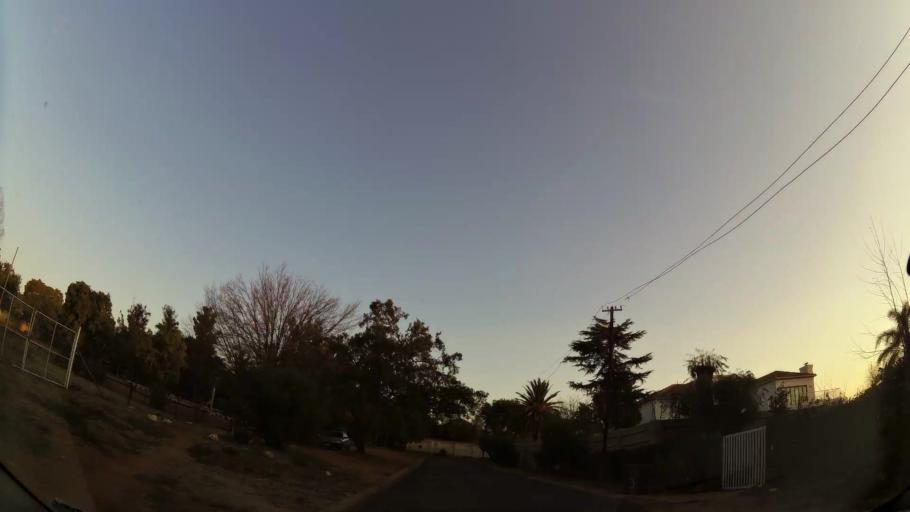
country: ZA
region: Gauteng
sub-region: City of Johannesburg Metropolitan Municipality
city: Johannesburg
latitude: -26.1203
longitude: 27.9926
